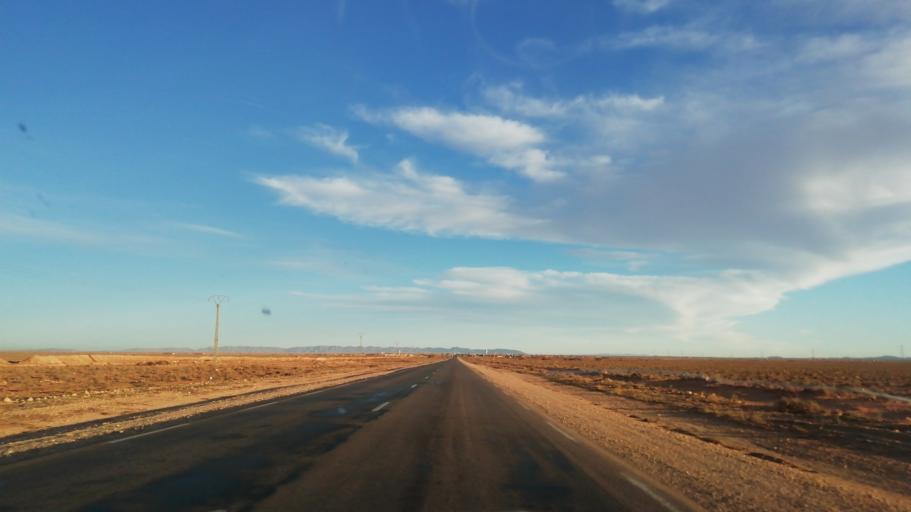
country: DZ
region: Wilaya de Naama
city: Naama
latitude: 33.7330
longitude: -0.7573
